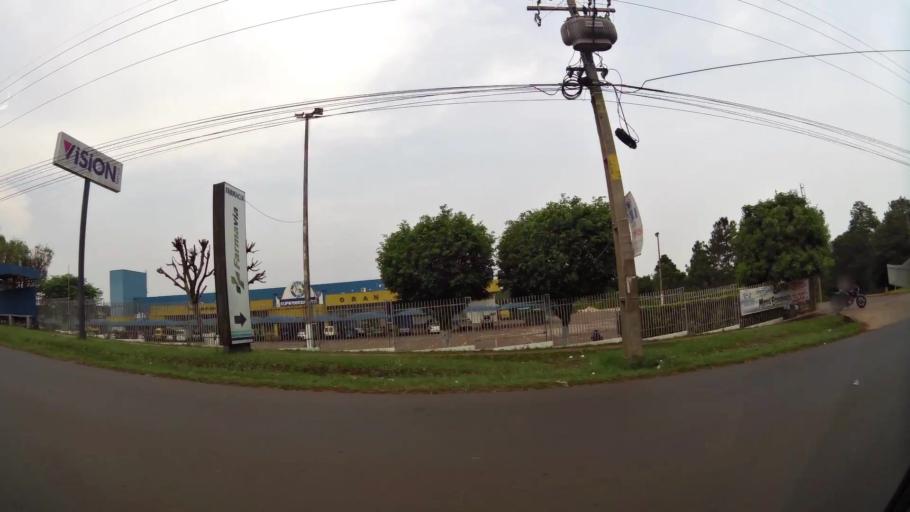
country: PY
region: Alto Parana
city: Presidente Franco
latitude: -25.5462
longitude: -54.6088
